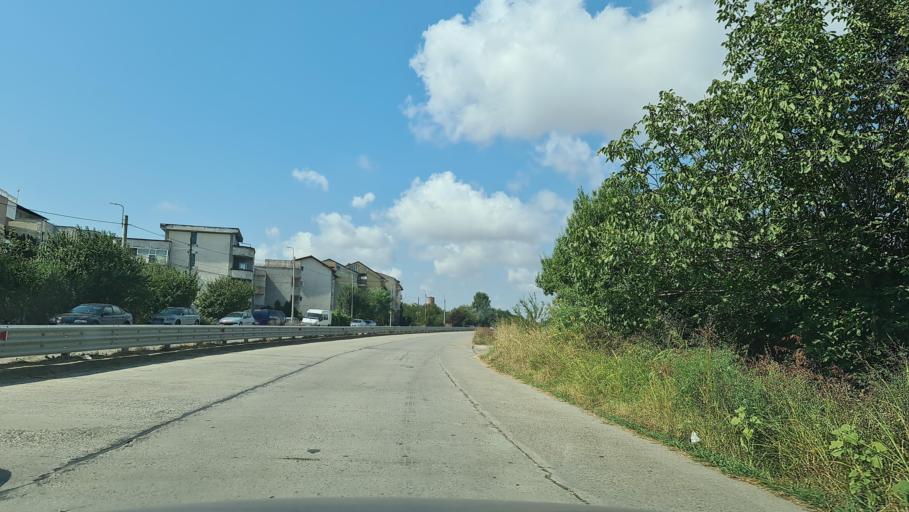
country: RO
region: Constanta
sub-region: Oras Eforie
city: Eforie Nord
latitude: 44.0777
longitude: 28.6369
